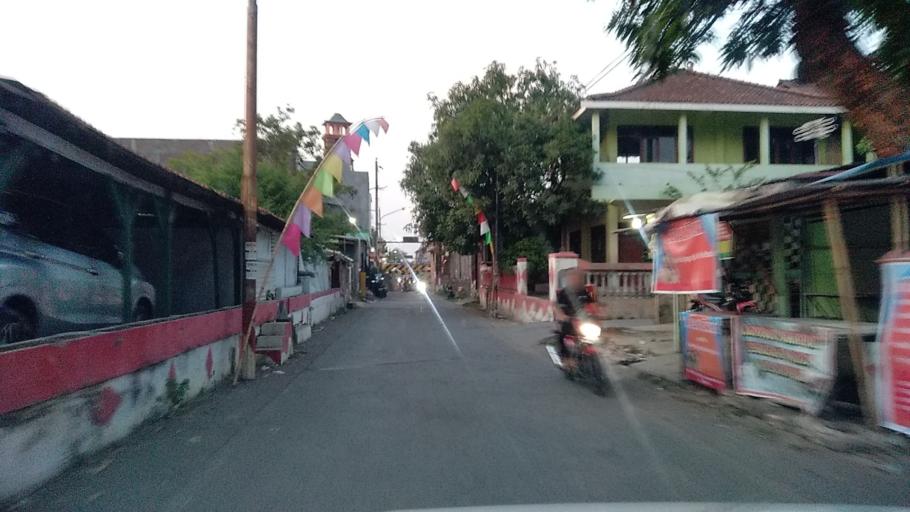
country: ID
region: Central Java
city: Semarang
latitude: -6.9766
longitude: 110.3313
